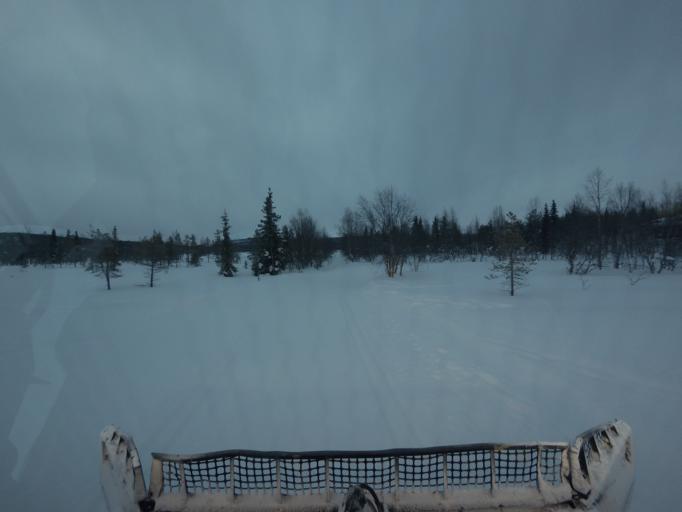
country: FI
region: Lapland
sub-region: Tunturi-Lappi
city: Kolari
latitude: 67.6143
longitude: 24.1544
